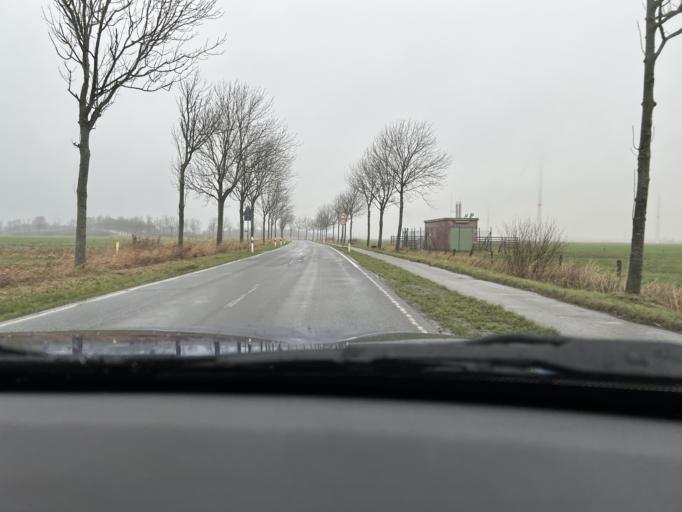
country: DE
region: Schleswig-Holstein
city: Stelle-Wittenwurth
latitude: 54.2391
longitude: 9.0448
